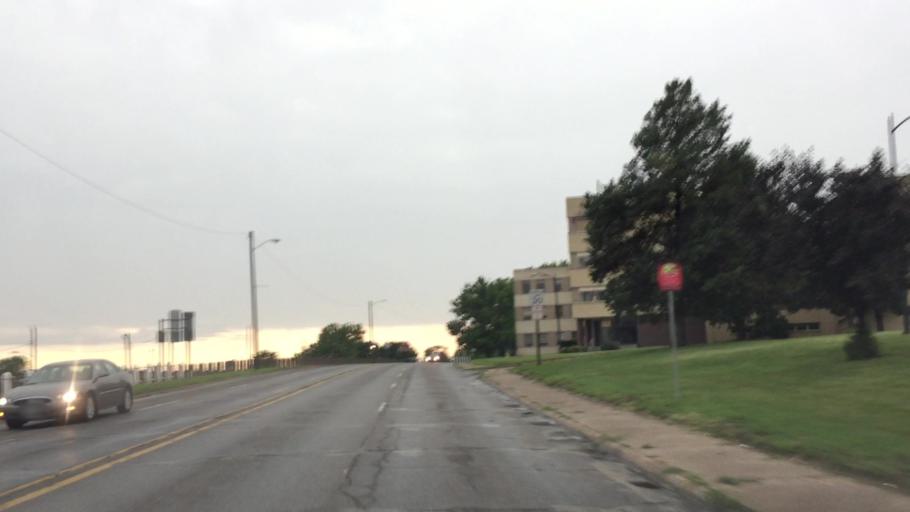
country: US
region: Iowa
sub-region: Lee County
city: Fort Madison
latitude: 40.6302
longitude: -91.3014
